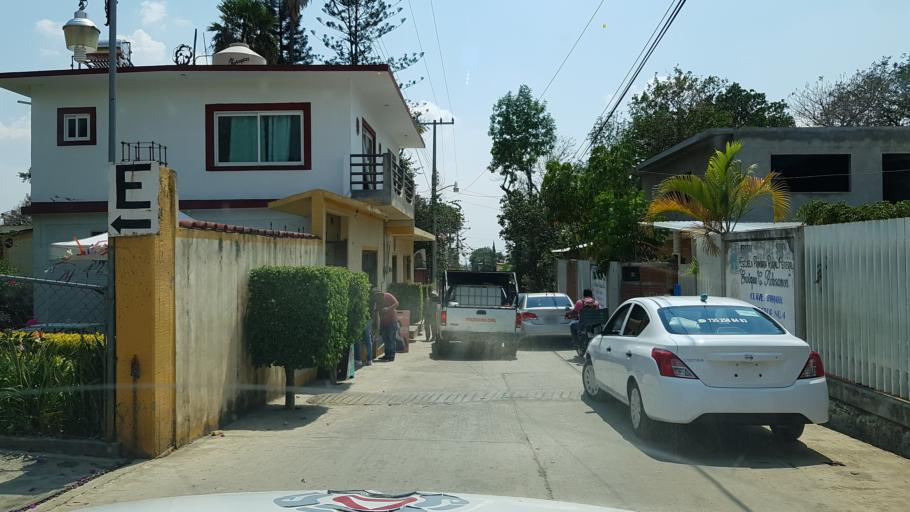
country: MX
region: Morelos
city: Ocuituco
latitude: 18.8837
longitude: -98.8177
